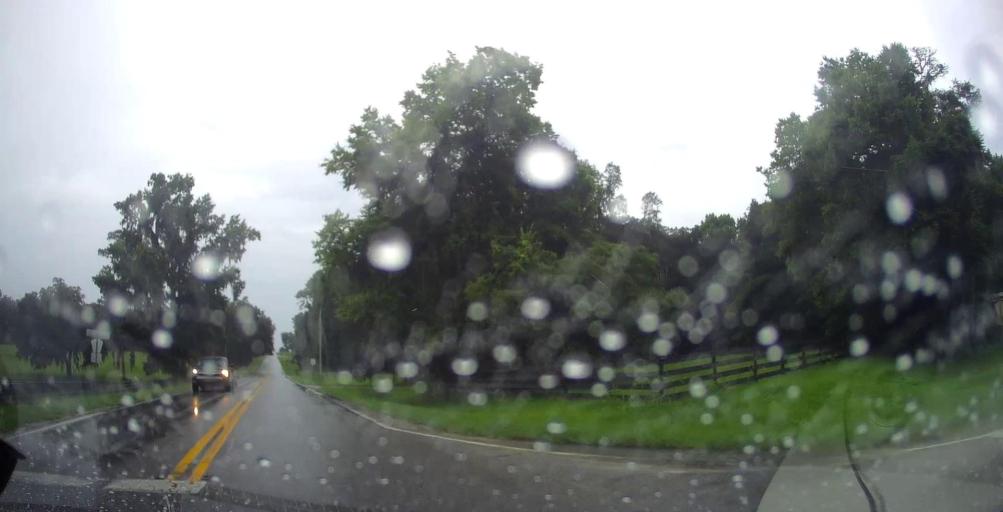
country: US
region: Florida
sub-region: Marion County
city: Citra
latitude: 29.3609
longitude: -82.2514
